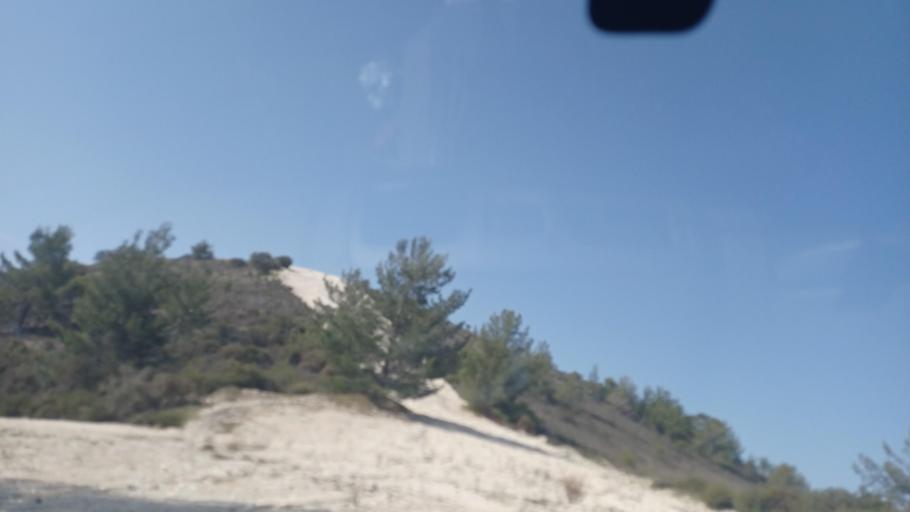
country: CY
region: Limassol
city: Pachna
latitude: 34.8873
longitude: 32.7286
